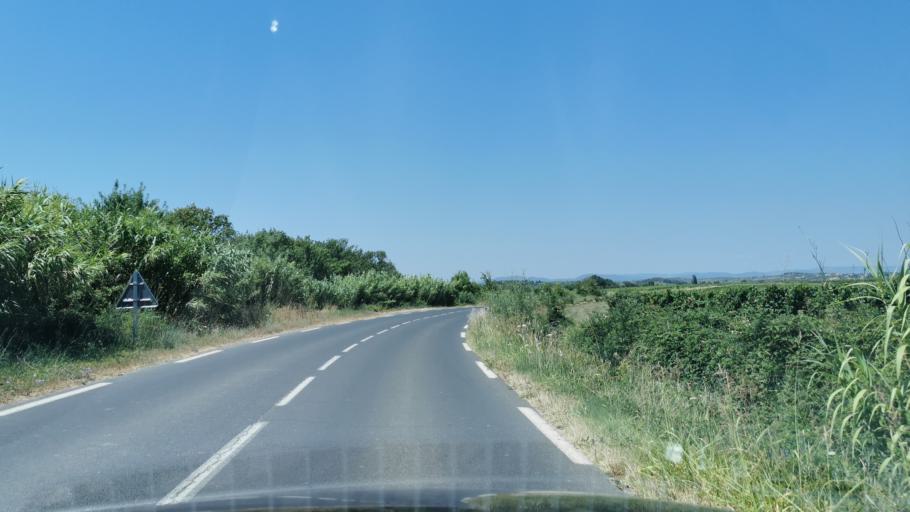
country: FR
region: Languedoc-Roussillon
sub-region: Departement de l'Herault
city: Maureilhan
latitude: 43.3646
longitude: 3.1183
